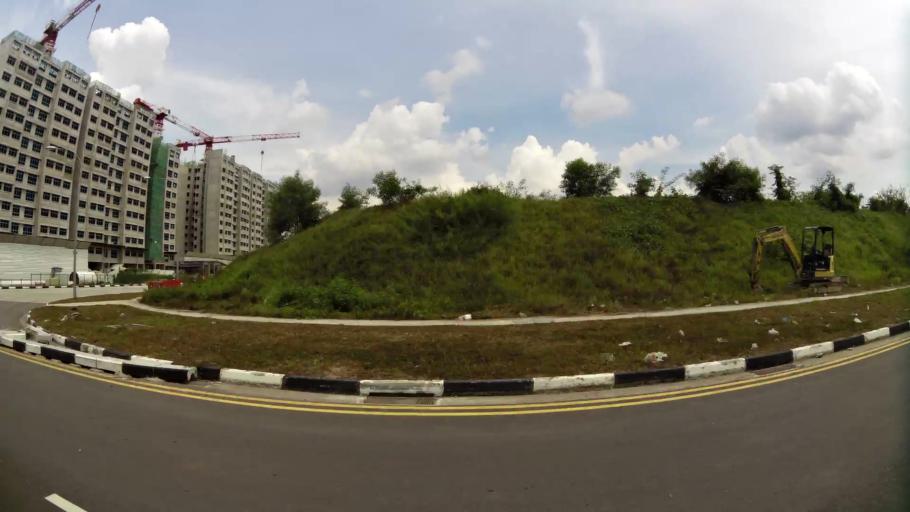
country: MY
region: Johor
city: Johor Bahru
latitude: 1.3558
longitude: 103.7404
